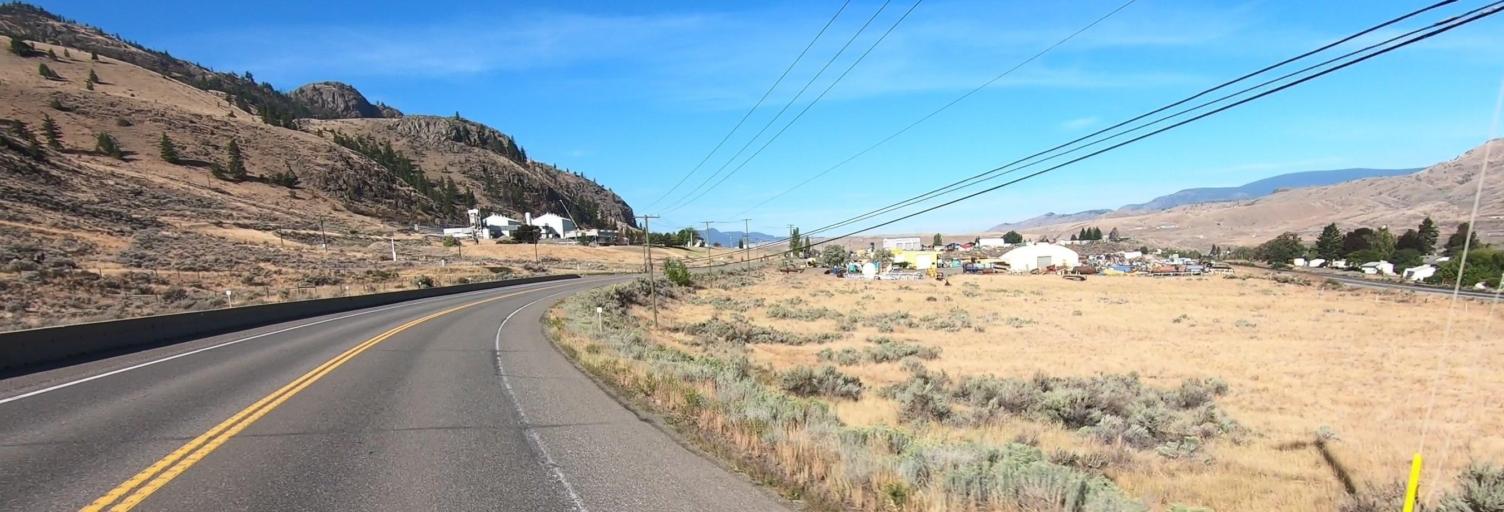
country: CA
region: British Columbia
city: Logan Lake
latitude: 50.7502
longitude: -120.8482
